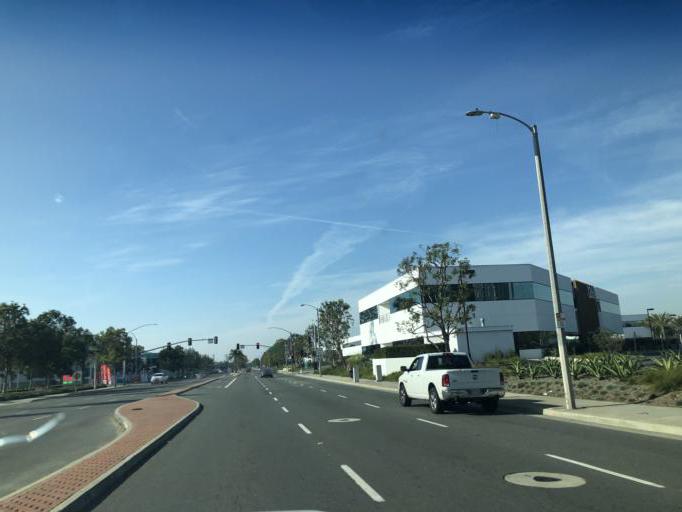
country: US
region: California
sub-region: Orange County
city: Santa Ana
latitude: 33.7087
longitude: -117.8548
